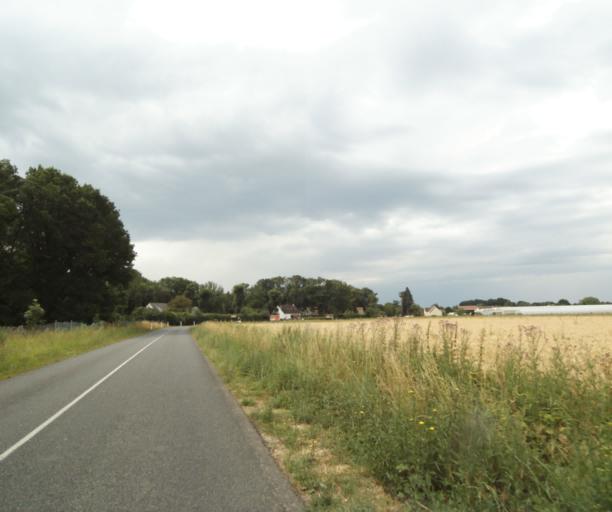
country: FR
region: Ile-de-France
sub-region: Departement de Seine-et-Marne
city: Saint-Sauveur-sur-Ecole
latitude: 48.5086
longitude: 2.5362
